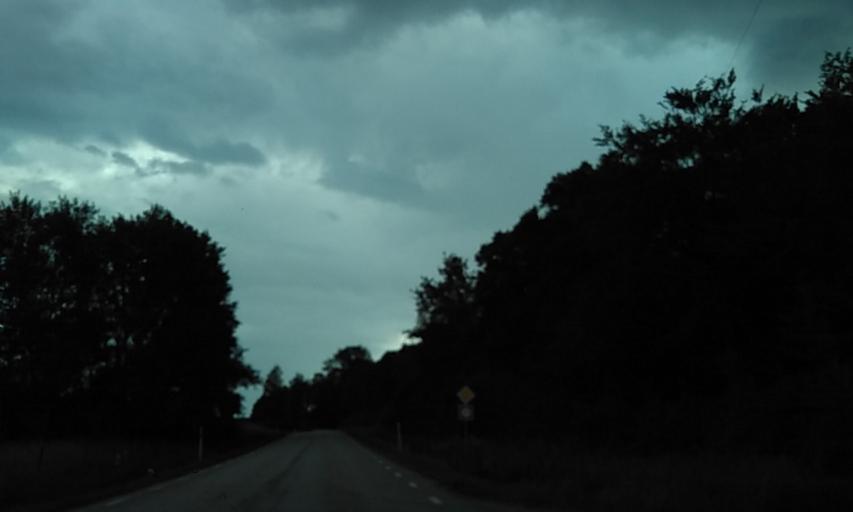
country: SE
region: Vaestra Goetaland
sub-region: Grastorps Kommun
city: Graestorp
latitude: 58.4720
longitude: 12.8220
